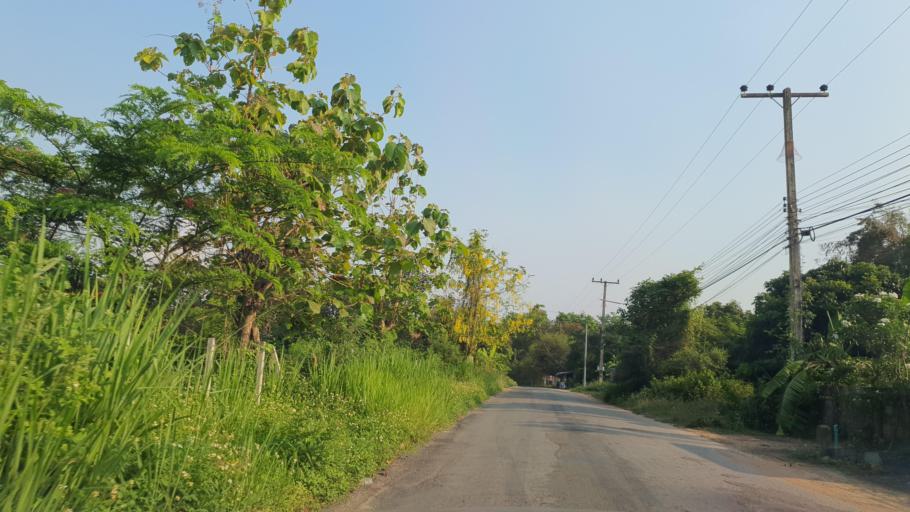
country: TH
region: Chiang Mai
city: Mae Wang
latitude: 18.6184
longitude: 98.8203
